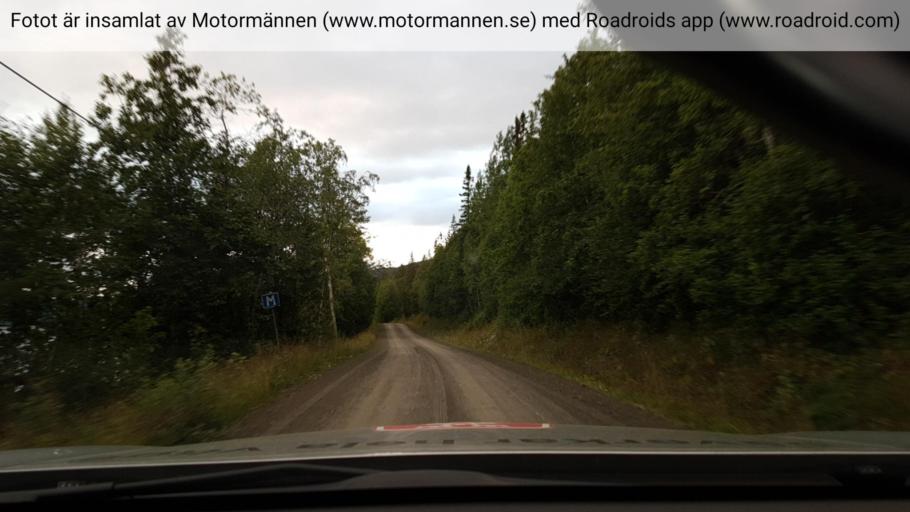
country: NO
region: Nordland
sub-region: Hattfjelldal
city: Hattfjelldal
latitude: 65.6244
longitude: 15.2357
